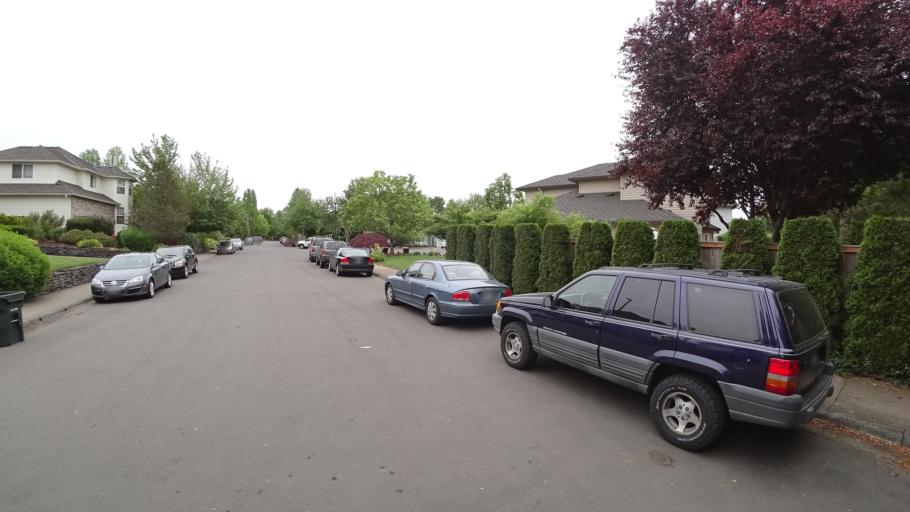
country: US
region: Oregon
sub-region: Washington County
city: Bethany
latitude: 45.5487
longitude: -122.8627
